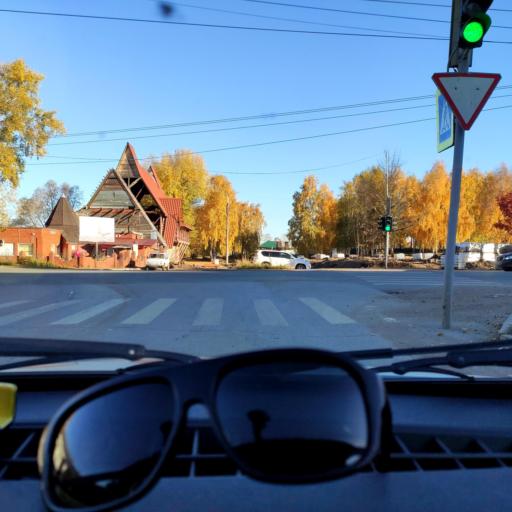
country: RU
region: Bashkortostan
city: Blagoveshchensk
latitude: 55.0317
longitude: 55.9715
